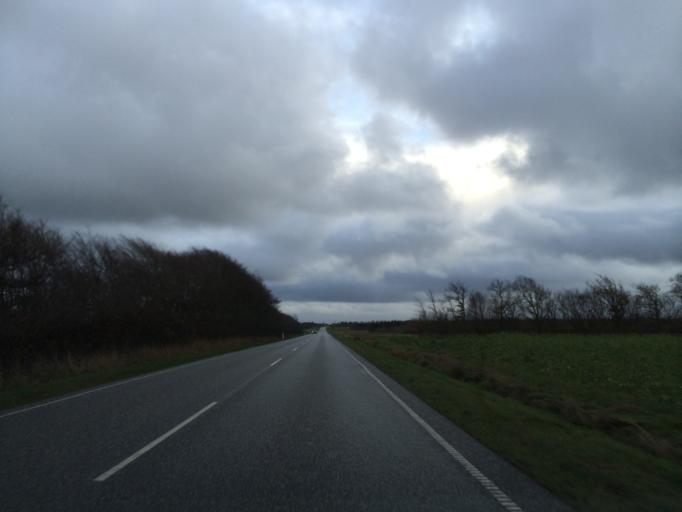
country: DK
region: Central Jutland
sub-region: Ringkobing-Skjern Kommune
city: Ringkobing
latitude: 56.1043
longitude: 8.3256
